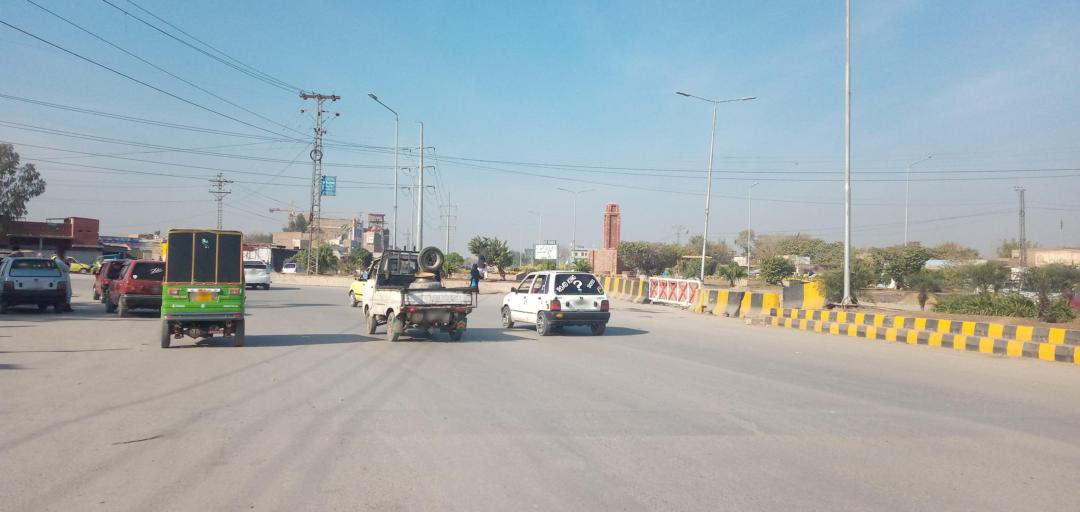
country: PK
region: Khyber Pakhtunkhwa
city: Peshawar
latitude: 33.9605
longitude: 71.5055
